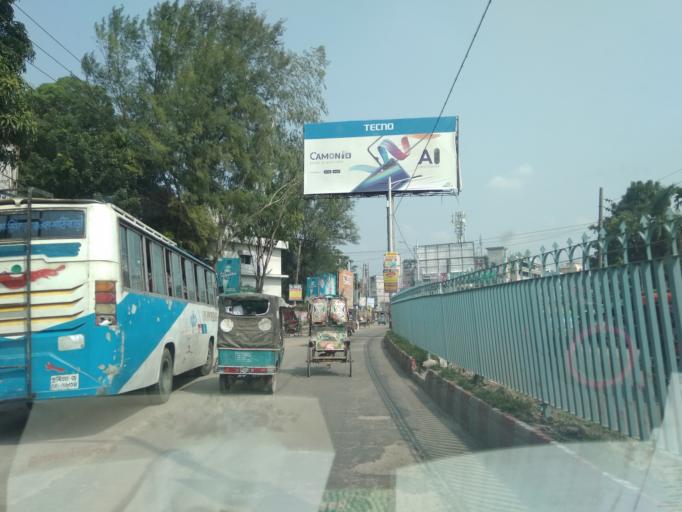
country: BD
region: Rangpur Division
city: Rangpur
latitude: 25.7662
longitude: 89.2306
